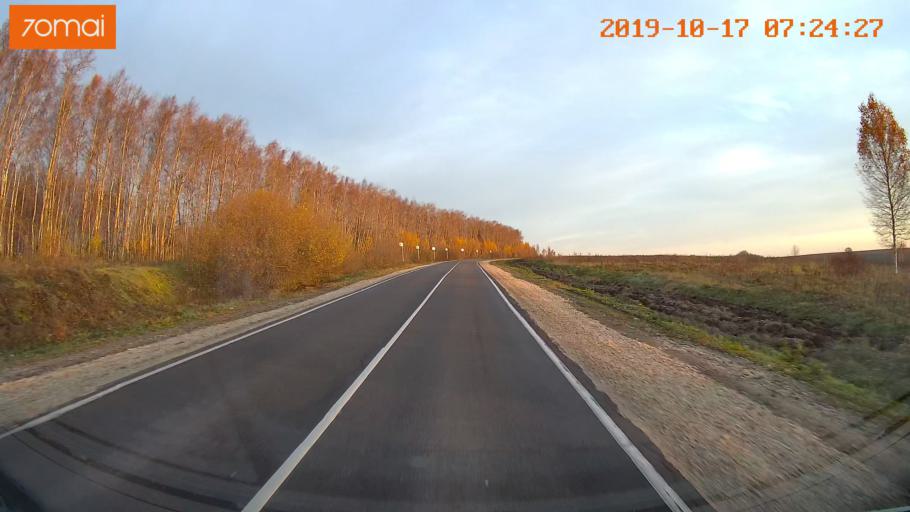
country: RU
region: Ivanovo
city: Gavrilov Posad
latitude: 56.3385
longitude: 40.1121
